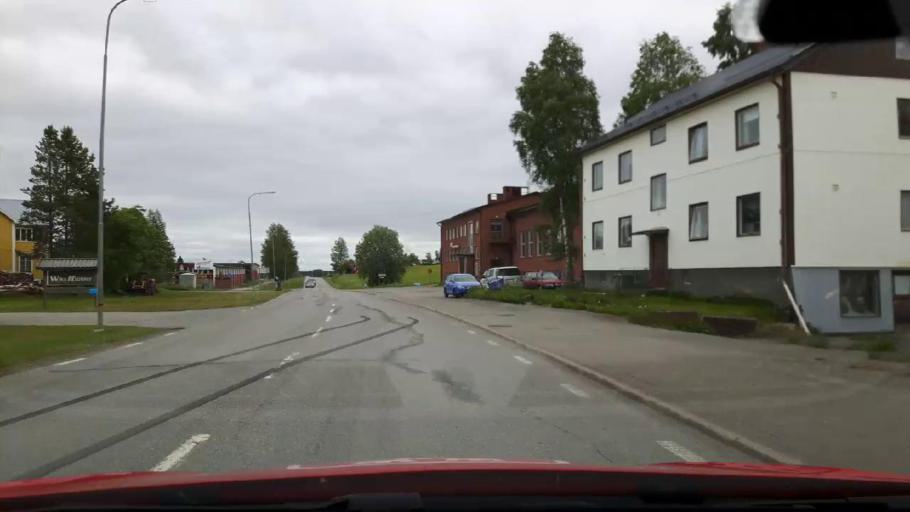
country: SE
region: Jaemtland
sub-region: Stroemsunds Kommun
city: Stroemsund
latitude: 63.5814
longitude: 15.3555
